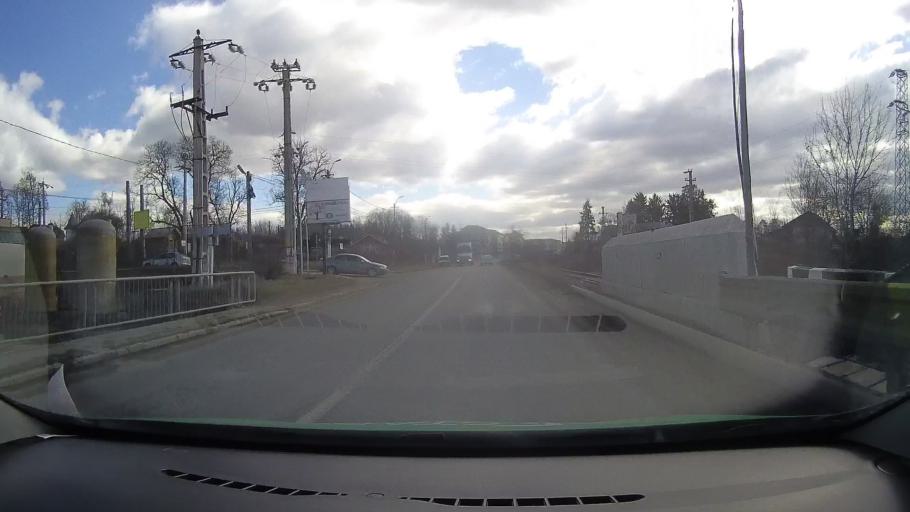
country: RO
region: Dambovita
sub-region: Oras Pucioasa
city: Pucioasa
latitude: 45.0812
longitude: 25.4256
